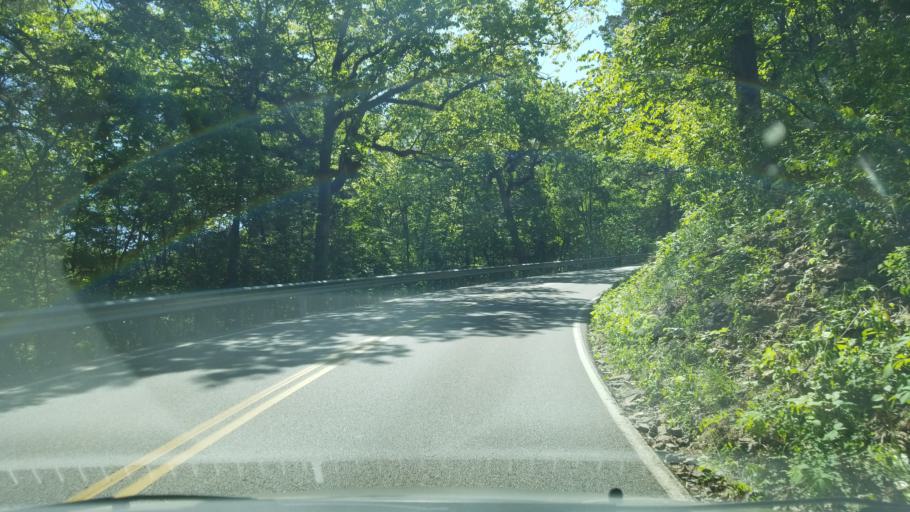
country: US
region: Tennessee
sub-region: Hamilton County
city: Middle Valley
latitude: 35.1700
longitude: -85.1753
